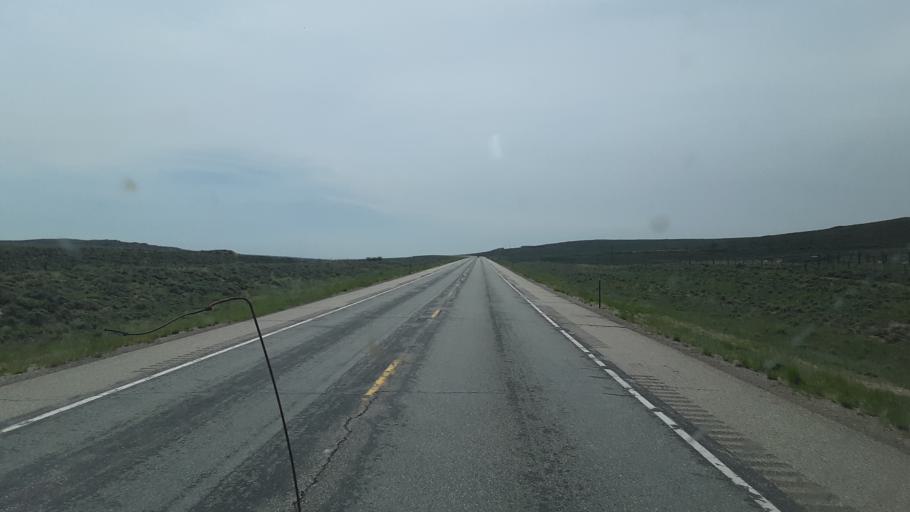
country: US
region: Wyoming
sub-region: Carbon County
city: Saratoga
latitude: 41.1144
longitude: -106.5312
